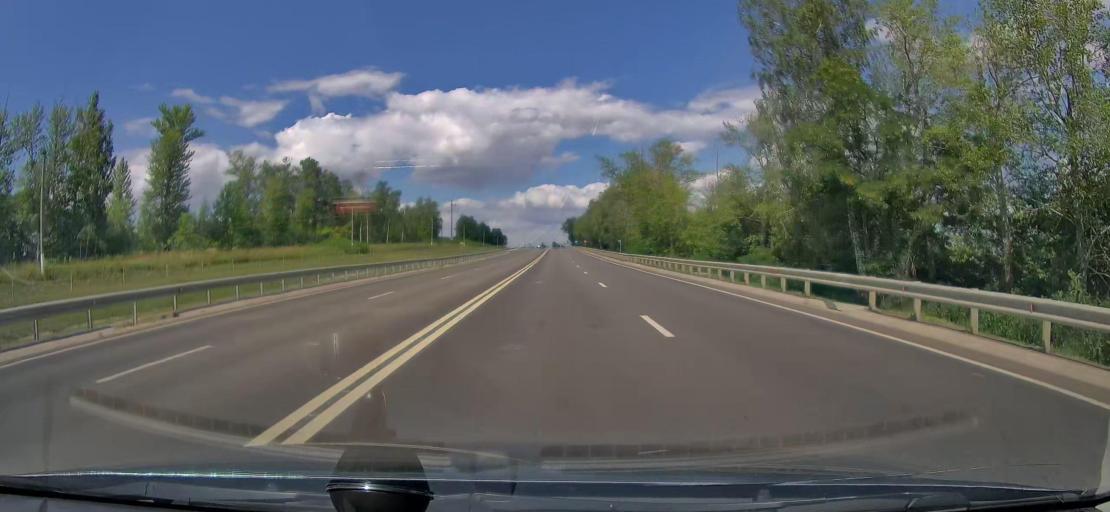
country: RU
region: Kursk
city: Zolotukhino
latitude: 51.9562
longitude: 36.3051
